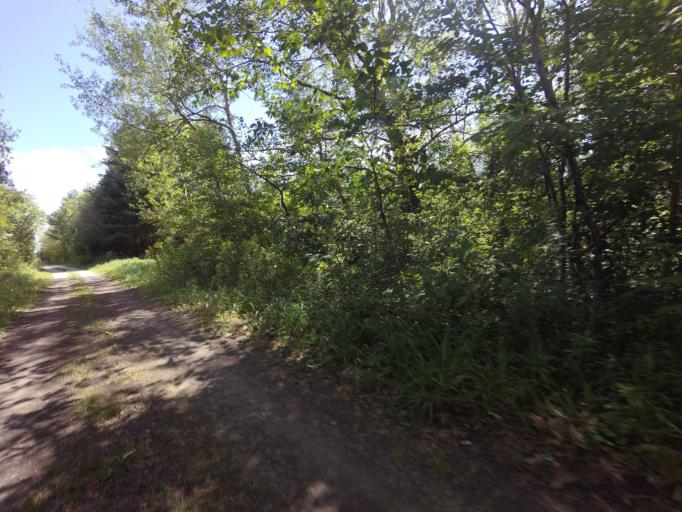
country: CA
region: Ontario
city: Orangeville
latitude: 43.7789
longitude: -80.1244
